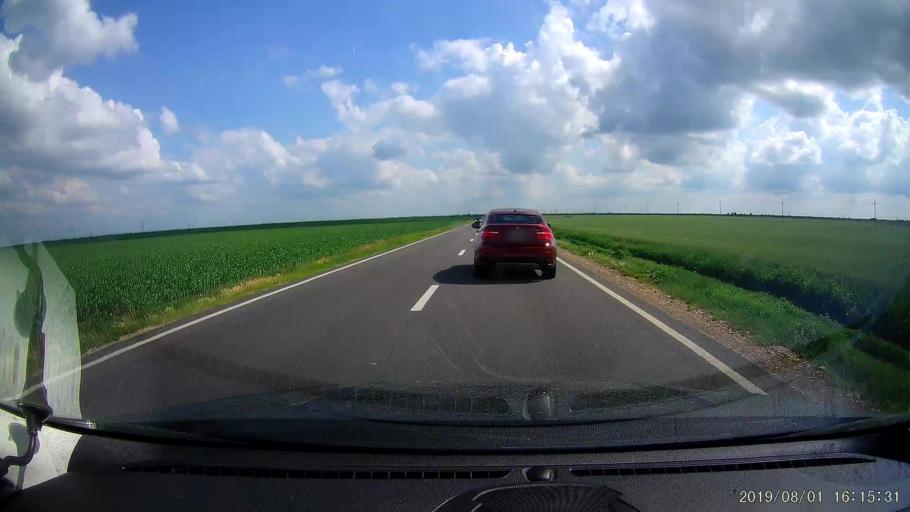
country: RO
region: Calarasi
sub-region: Comuna Stefan Voda
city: Stefan Voda
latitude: 44.3363
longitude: 27.3609
